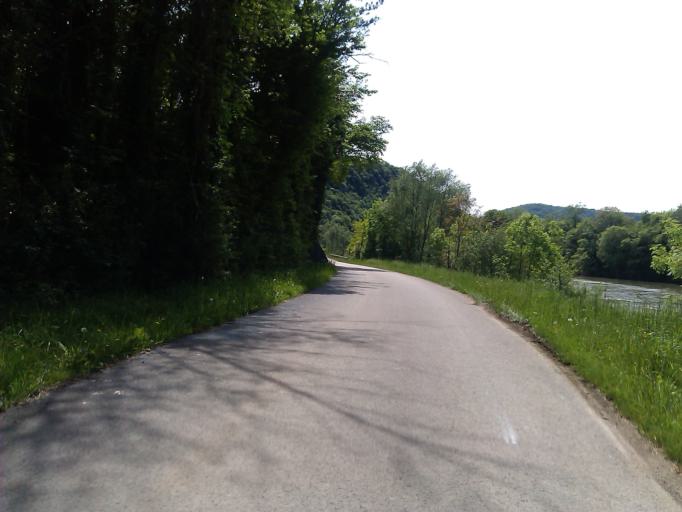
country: FR
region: Franche-Comte
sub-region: Departement du Doubs
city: Montferrand-le-Chateau
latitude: 47.1788
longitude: 5.9447
